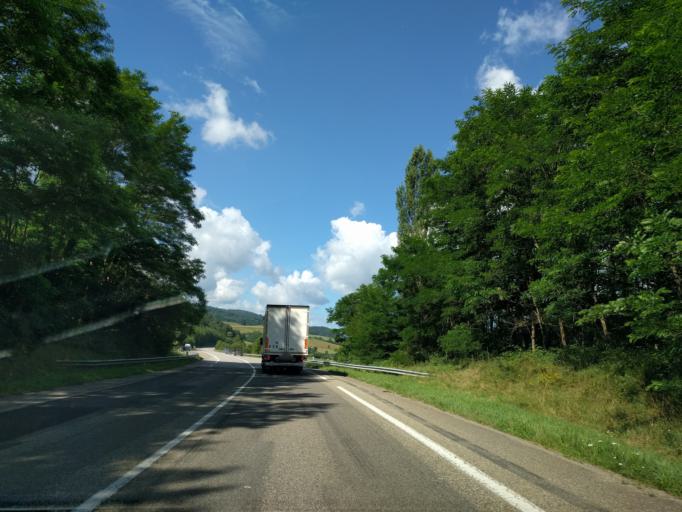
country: FR
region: Alsace
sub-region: Departement du Haut-Rhin
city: Liepvre
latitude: 48.2684
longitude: 7.2590
